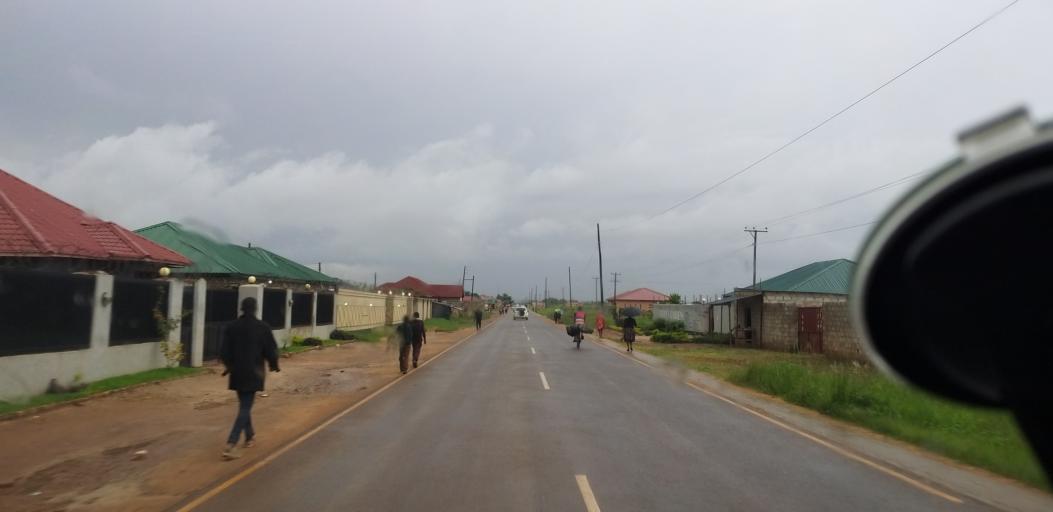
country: ZM
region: Lusaka
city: Lusaka
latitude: -15.5076
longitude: 28.3118
